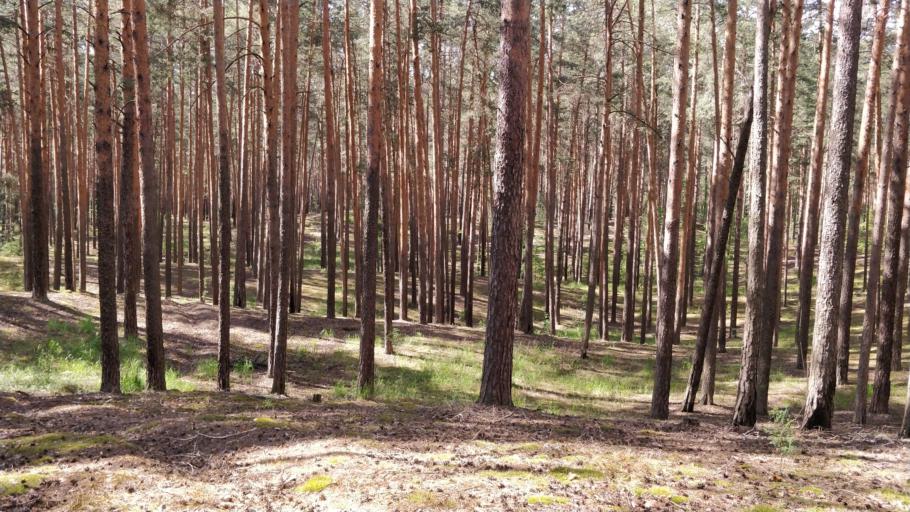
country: RU
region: Perm
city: Perm
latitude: 58.0715
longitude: 56.3046
